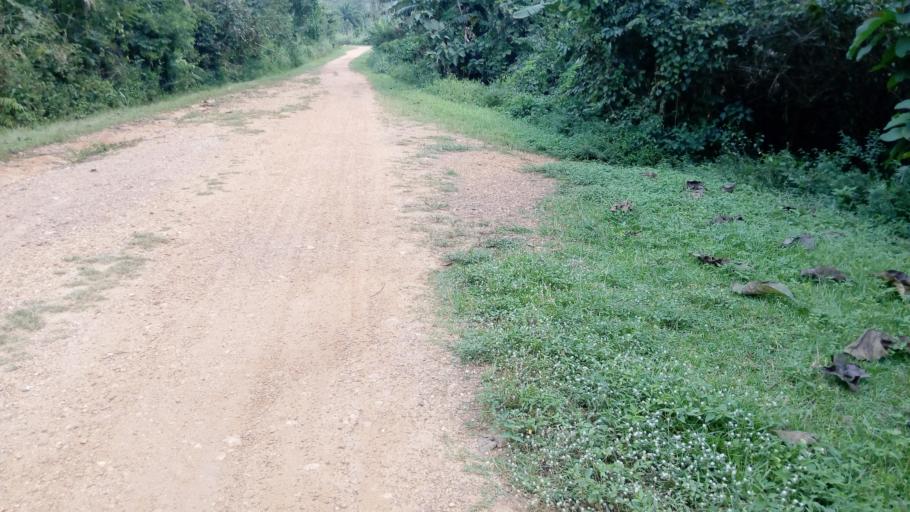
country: TG
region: Plateaux
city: Badou
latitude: 7.6621
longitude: 0.7280
